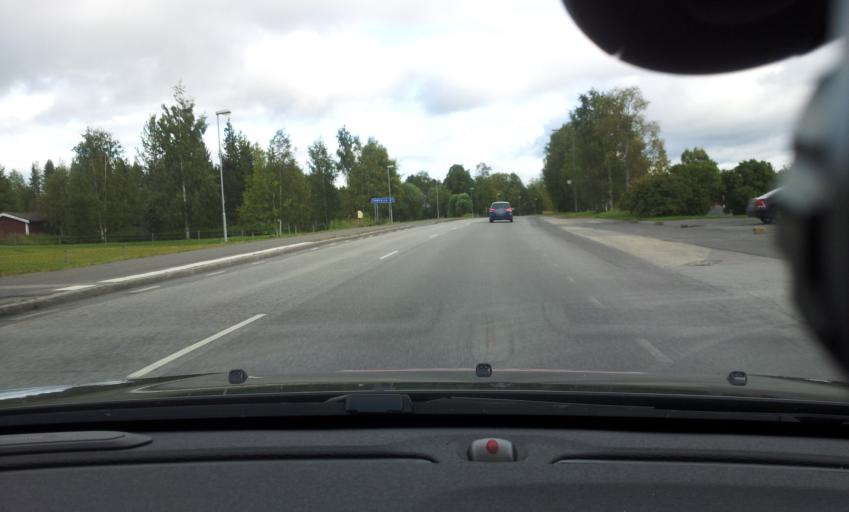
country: SE
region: Jaemtland
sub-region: OEstersunds Kommun
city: Ostersund
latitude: 63.1412
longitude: 14.7373
